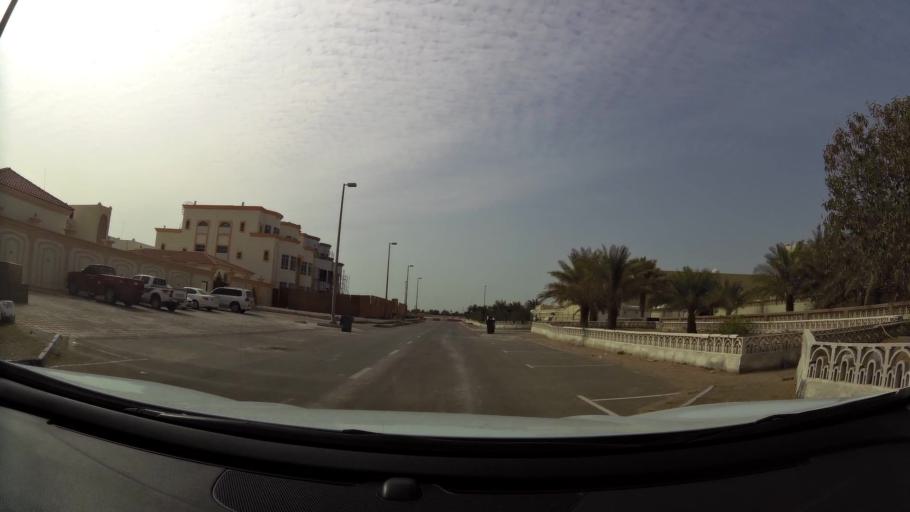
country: AE
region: Abu Dhabi
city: Abu Dhabi
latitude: 24.5946
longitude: 54.6954
